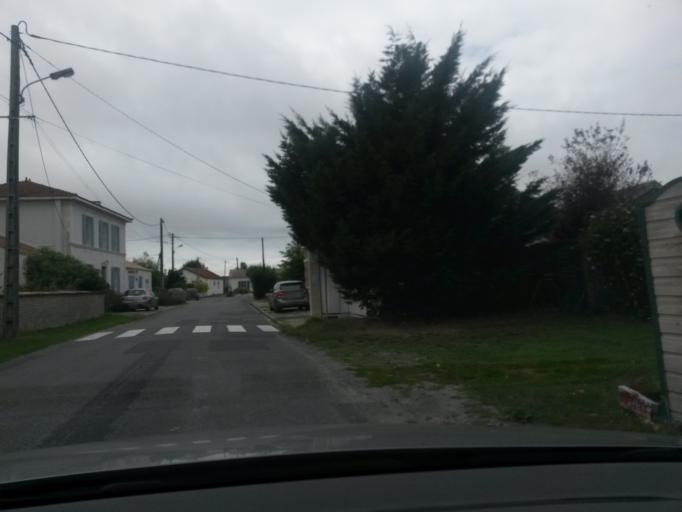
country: FR
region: Poitou-Charentes
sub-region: Departement de la Charente-Maritime
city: Saint-Trojan-les-Bains
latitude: 45.8739
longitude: -1.2140
